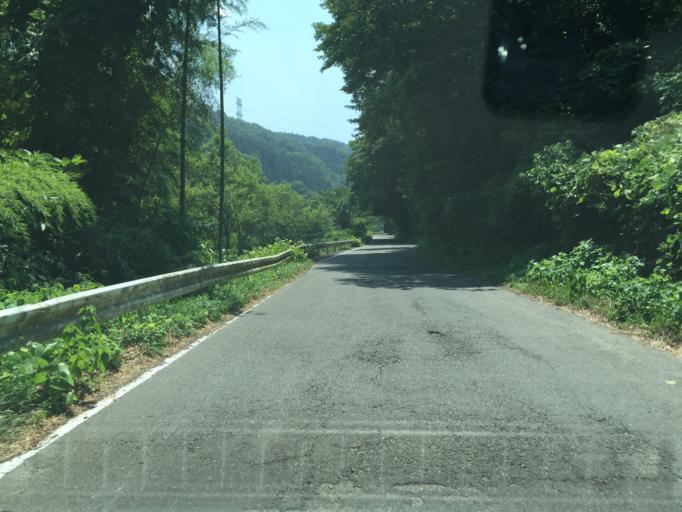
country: JP
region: Miyagi
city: Marumori
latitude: 37.9189
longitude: 140.6878
